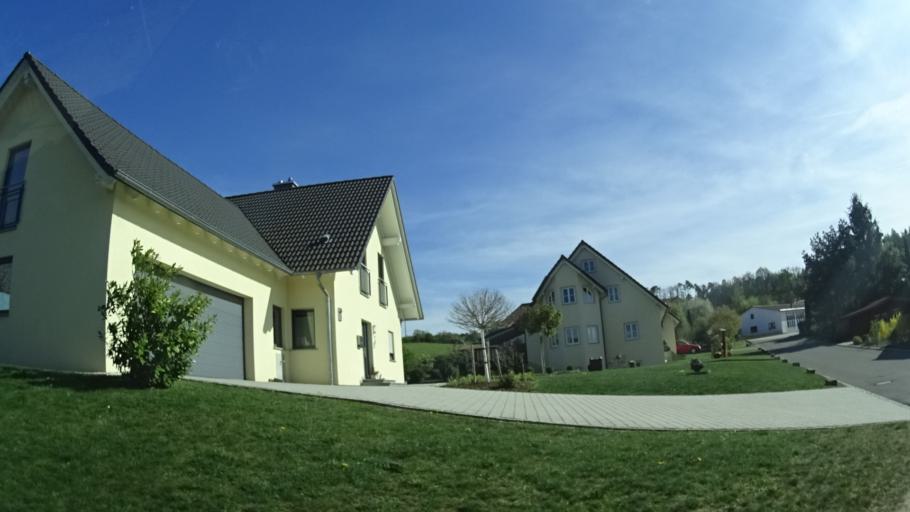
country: DE
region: Bavaria
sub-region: Regierungsbezirk Unterfranken
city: Burgpreppach
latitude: 50.0977
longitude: 10.6671
